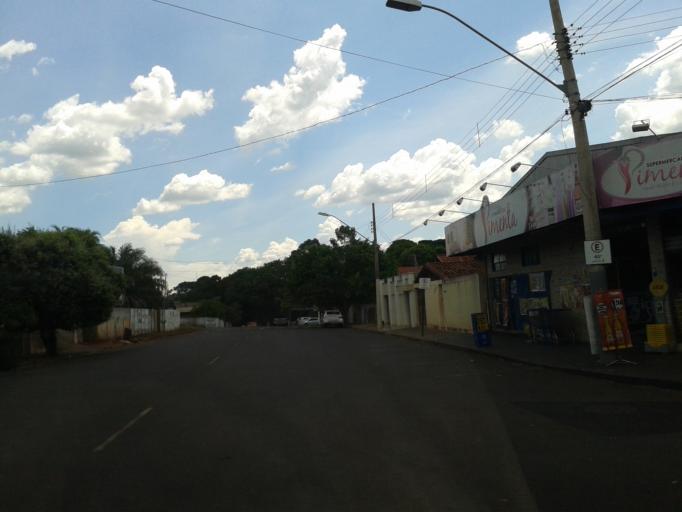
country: BR
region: Minas Gerais
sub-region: Ituiutaba
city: Ituiutaba
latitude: -18.9828
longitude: -49.4728
